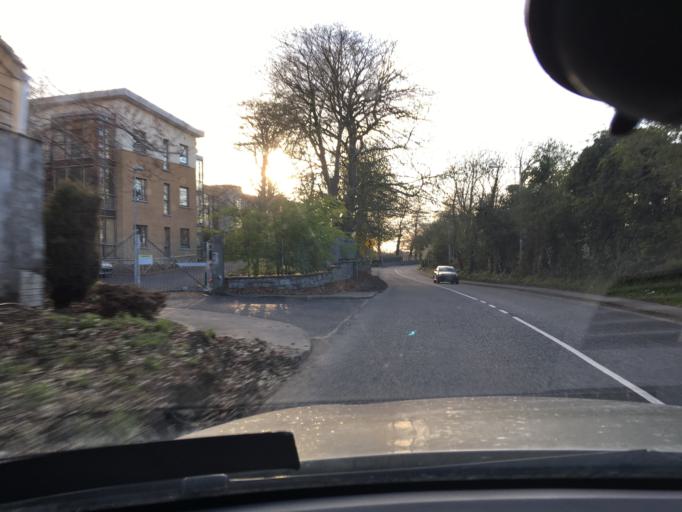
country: IE
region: Leinster
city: Hartstown
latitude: 53.4044
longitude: -6.4026
